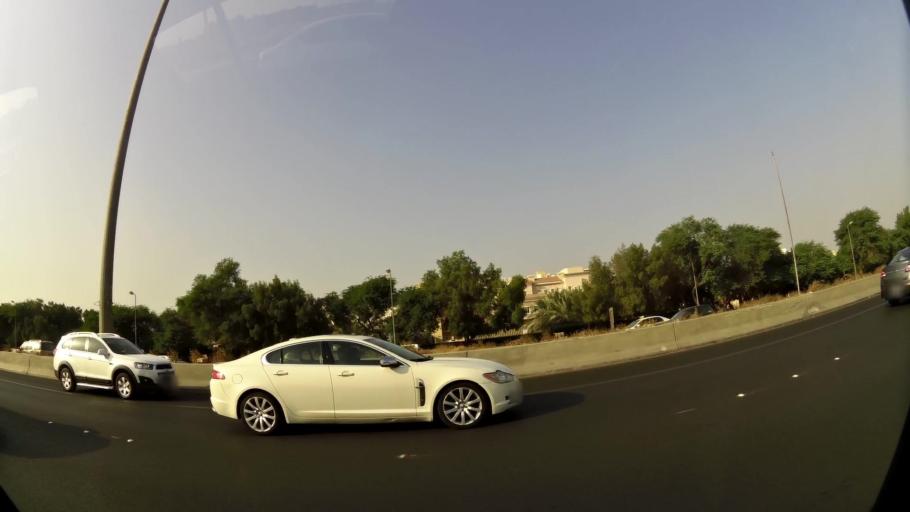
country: KW
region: Al Farwaniyah
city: Janub as Surrah
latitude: 29.3043
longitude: 47.9867
